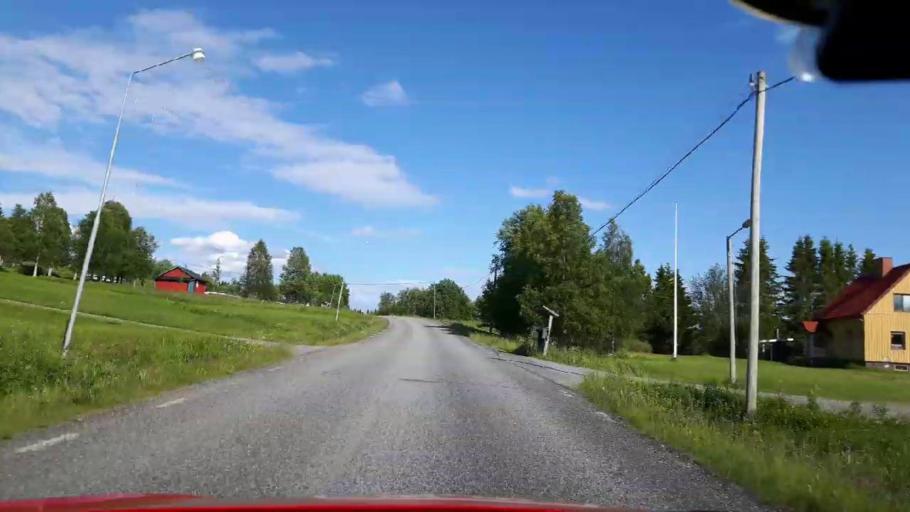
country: SE
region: Jaemtland
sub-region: Krokoms Kommun
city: Valla
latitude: 63.6990
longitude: 14.1608
